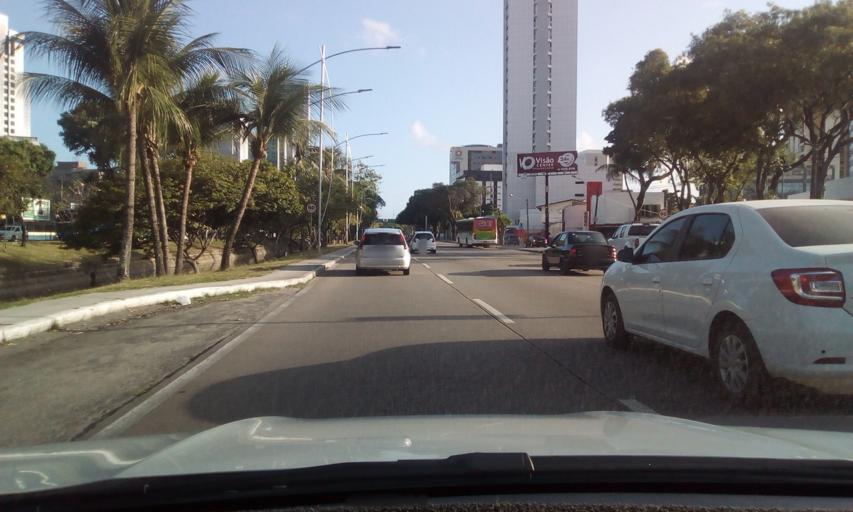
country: BR
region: Pernambuco
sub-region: Recife
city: Recife
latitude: -8.0596
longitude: -34.8980
